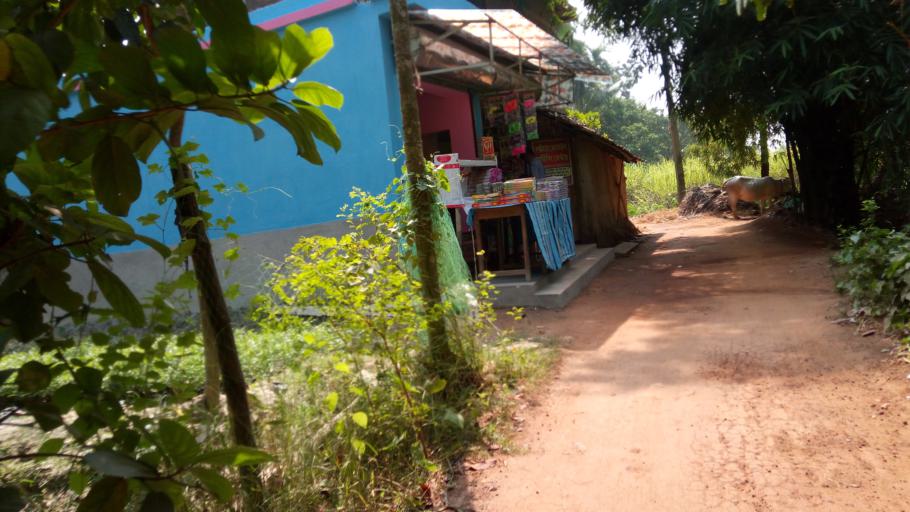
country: IN
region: West Bengal
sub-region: Purba Medinipur
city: Mahishadal
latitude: 22.1729
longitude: 87.9116
